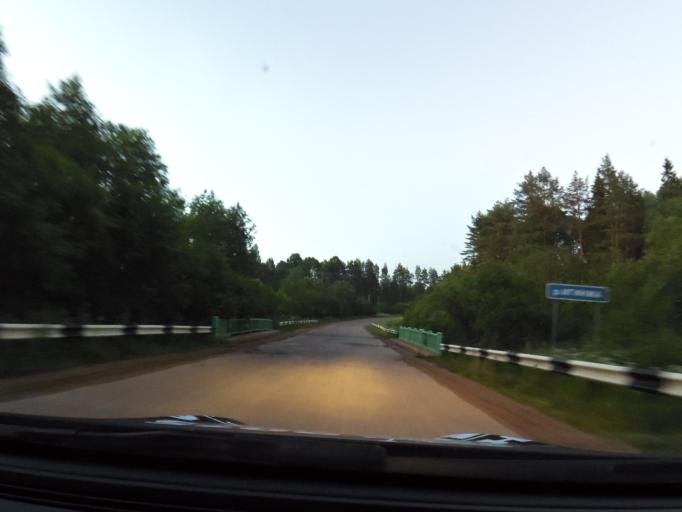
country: RU
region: Vologda
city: Vytegra
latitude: 61.0025
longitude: 36.3074
